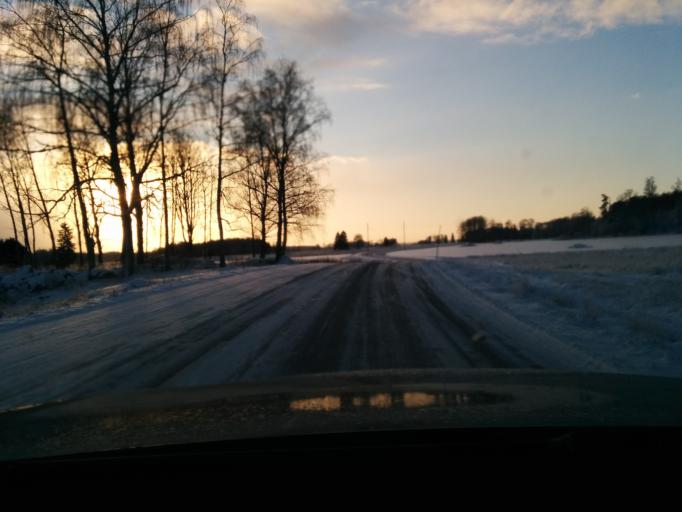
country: SE
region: Uppsala
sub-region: Tierps Kommun
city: Orbyhus
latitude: 60.1884
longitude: 17.6774
